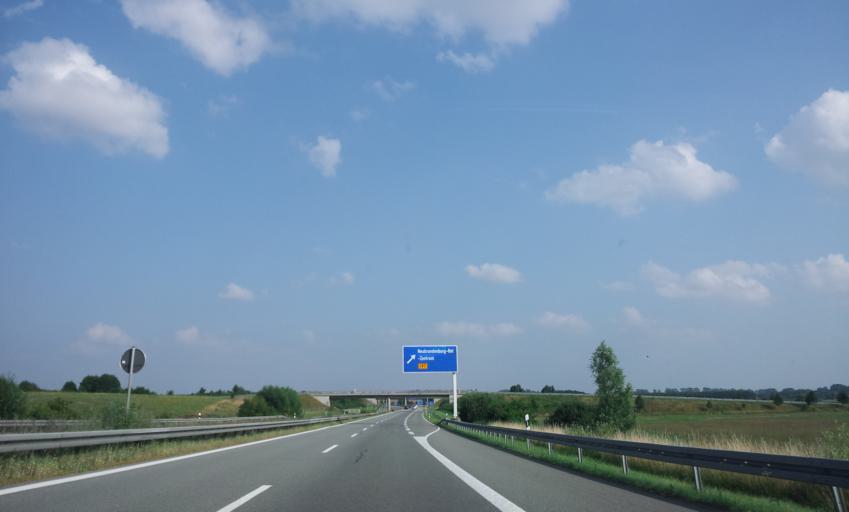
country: DE
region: Mecklenburg-Vorpommern
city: Neuenkirchen
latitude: 53.5865
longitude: 13.4121
